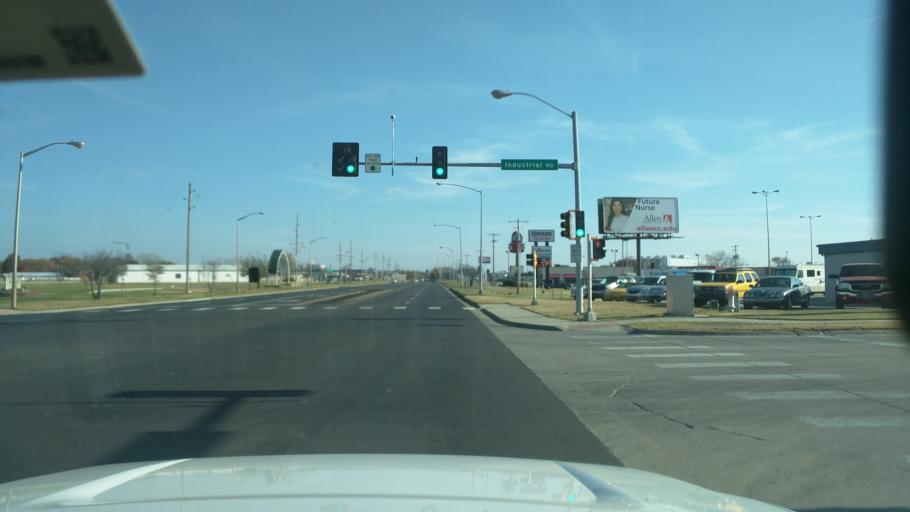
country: US
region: Kansas
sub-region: Lyon County
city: Emporia
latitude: 38.4085
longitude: -96.2174
